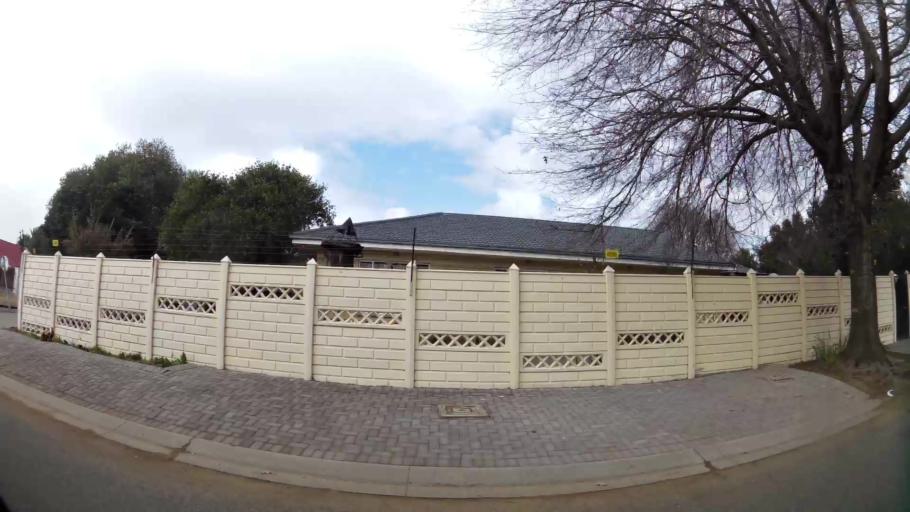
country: ZA
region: Gauteng
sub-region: Sedibeng District Municipality
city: Vanderbijlpark
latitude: -26.7148
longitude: 27.8569
